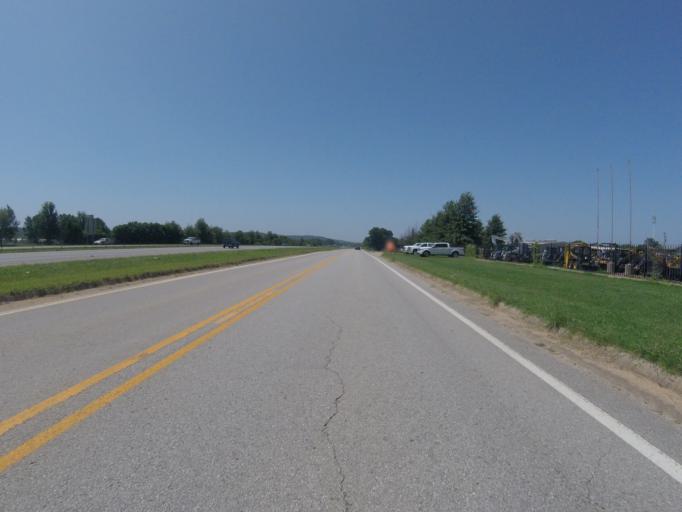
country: US
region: Arkansas
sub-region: Washington County
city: Johnson
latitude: 36.0975
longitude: -94.1874
